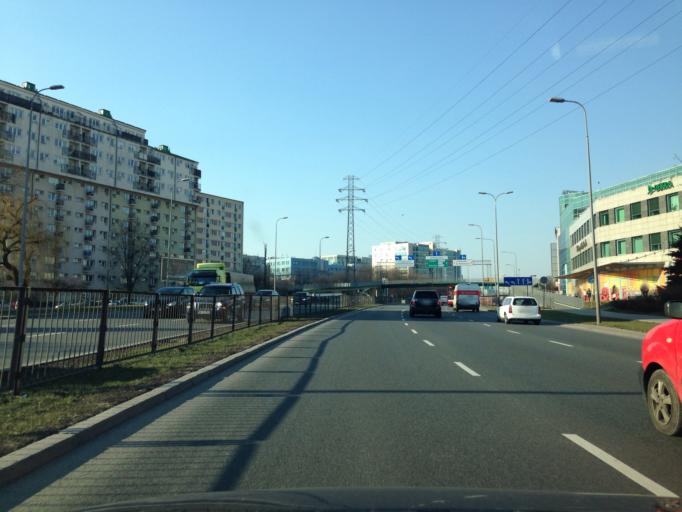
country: PL
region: Masovian Voivodeship
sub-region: Warszawa
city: Mokotow
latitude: 52.1732
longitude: 21.0033
